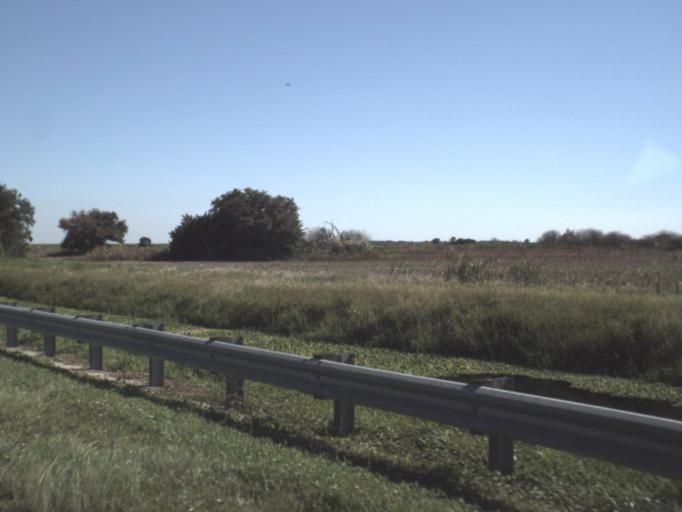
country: US
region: Florida
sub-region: Glades County
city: Moore Haven
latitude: 26.7550
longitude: -81.1500
